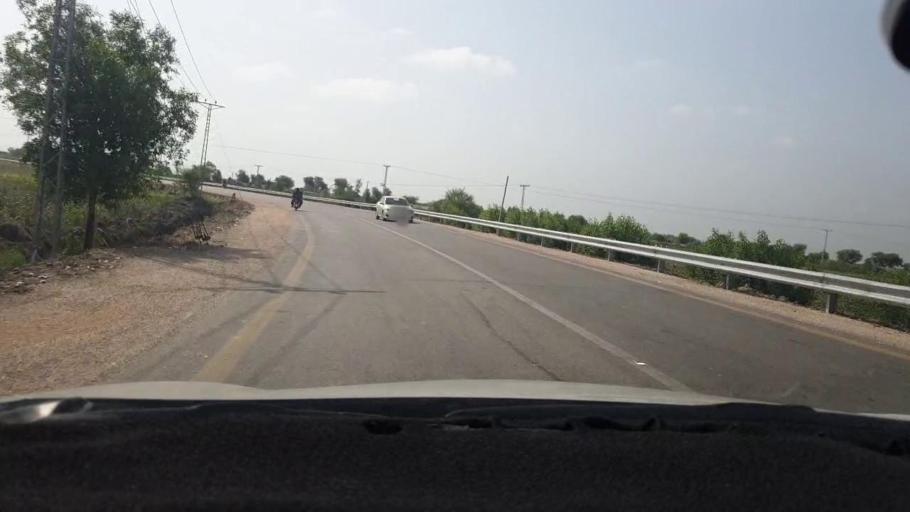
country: PK
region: Sindh
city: Mirpur Khas
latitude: 25.7675
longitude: 69.0713
